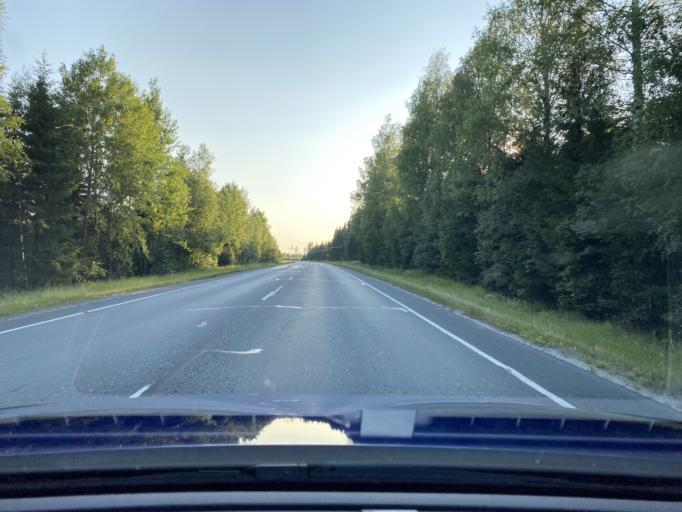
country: FI
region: Haeme
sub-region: Forssa
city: Tammela
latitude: 60.8289
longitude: 23.8843
